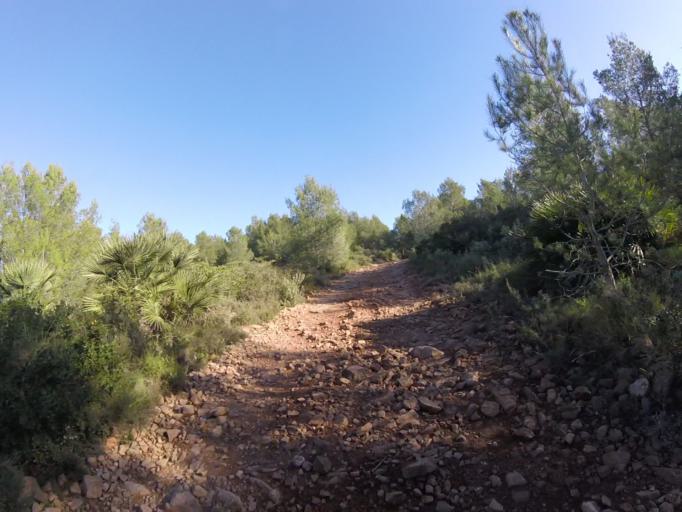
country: ES
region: Valencia
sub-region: Provincia de Castello
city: Benicassim
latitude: 40.0862
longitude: 0.0908
